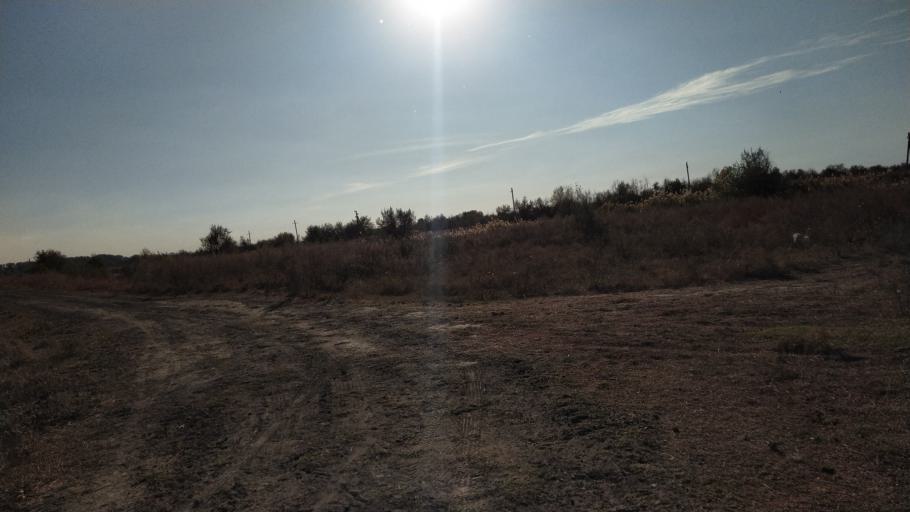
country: RU
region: Rostov
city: Kuleshovka
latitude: 47.1203
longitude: 39.6220
